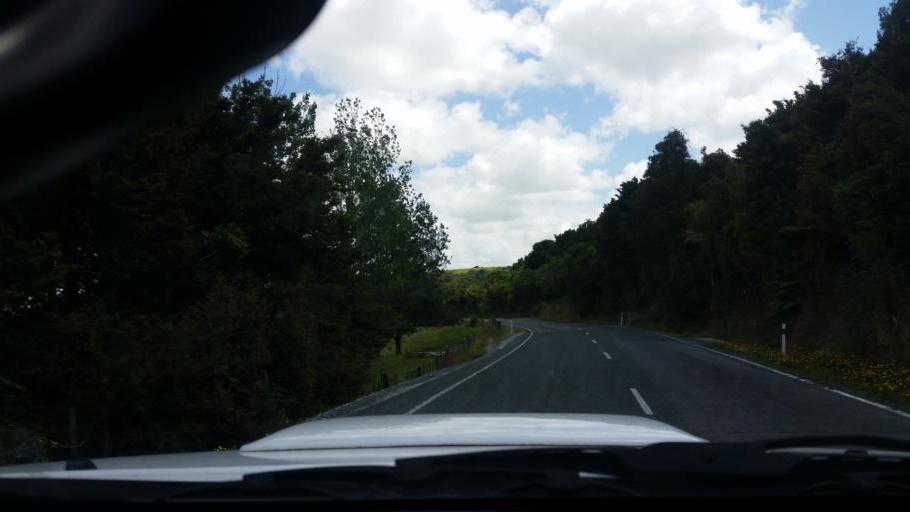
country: NZ
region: Northland
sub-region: Whangarei
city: Ruakaka
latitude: -36.0730
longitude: 174.2622
